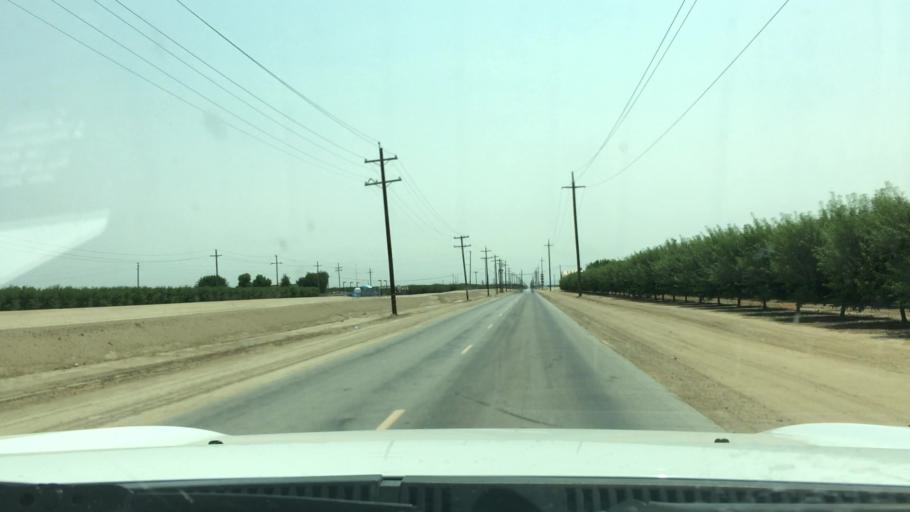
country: US
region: California
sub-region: Kern County
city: Wasco
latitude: 35.6121
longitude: -119.4380
